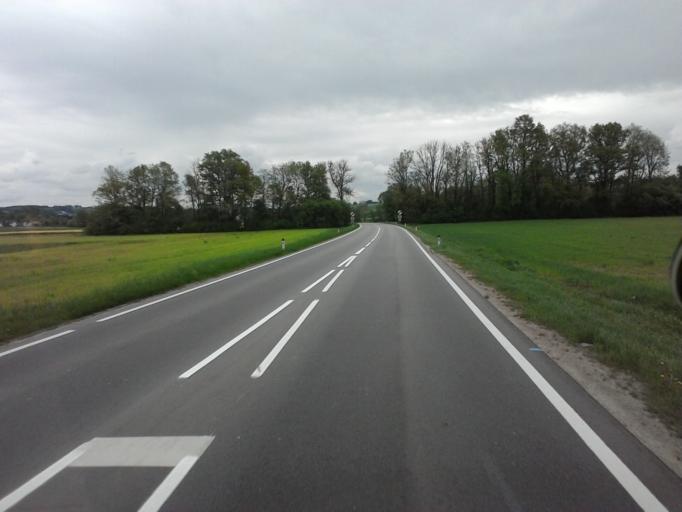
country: AT
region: Upper Austria
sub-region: Politischer Bezirk Grieskirchen
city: Grieskirchen
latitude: 48.2326
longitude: 13.7895
